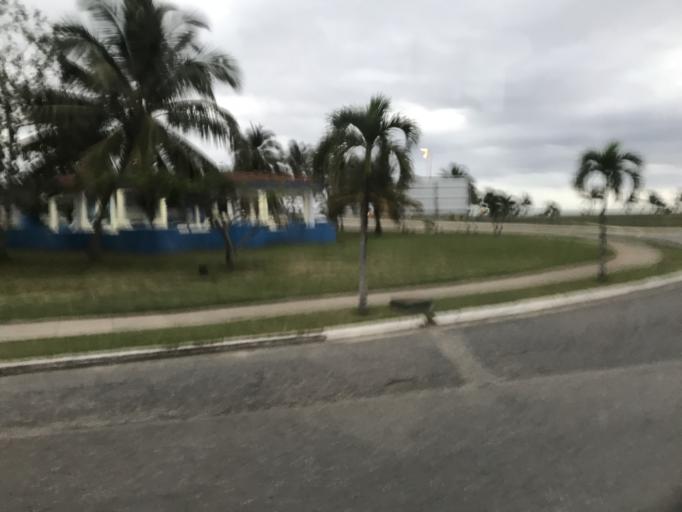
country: CU
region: Matanzas
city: Matanzas
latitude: 23.0364
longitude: -81.5652
